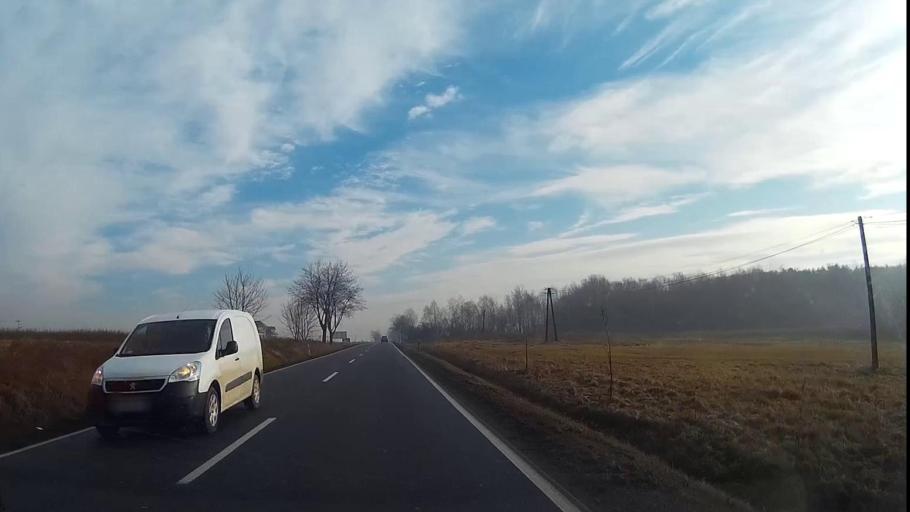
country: PL
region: Lesser Poland Voivodeship
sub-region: Powiat krakowski
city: Sanka
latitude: 50.0355
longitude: 19.6563
